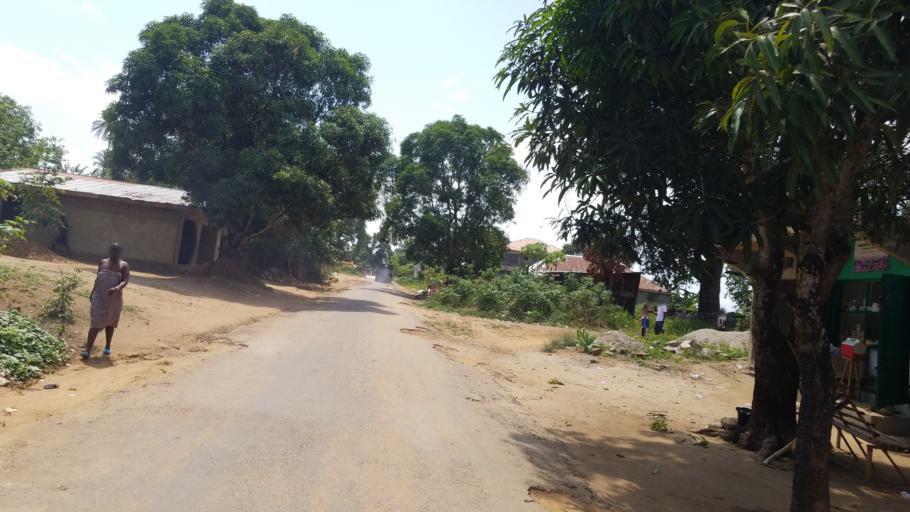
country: SL
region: Western Area
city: Waterloo
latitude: 8.3077
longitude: -13.0513
